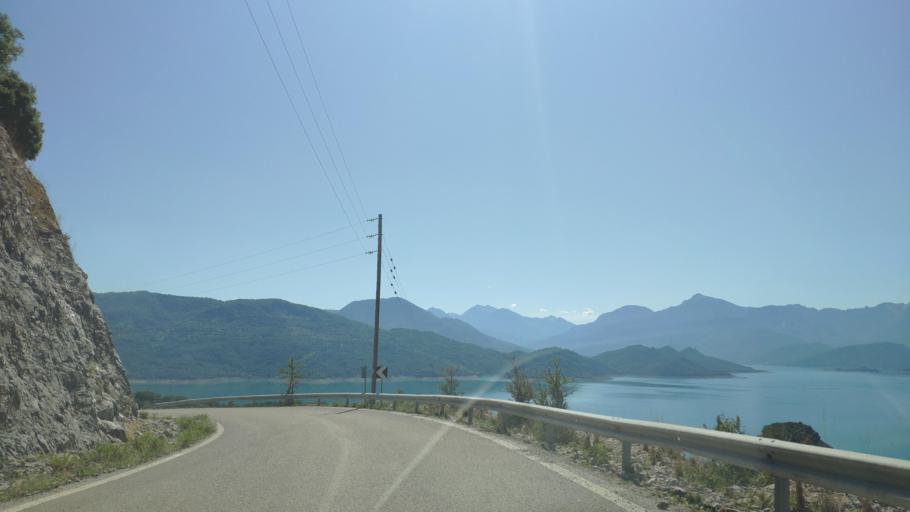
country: GR
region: Central Greece
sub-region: Nomos Evrytanias
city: Kerasochori
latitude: 38.9653
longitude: 21.4775
